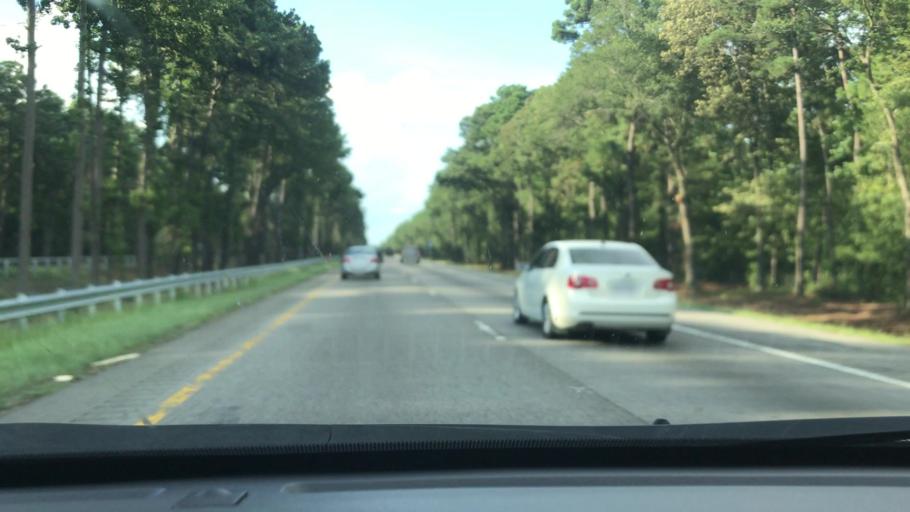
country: US
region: North Carolina
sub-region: Robeson County
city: Lumberton
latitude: 34.6791
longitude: -79.0029
